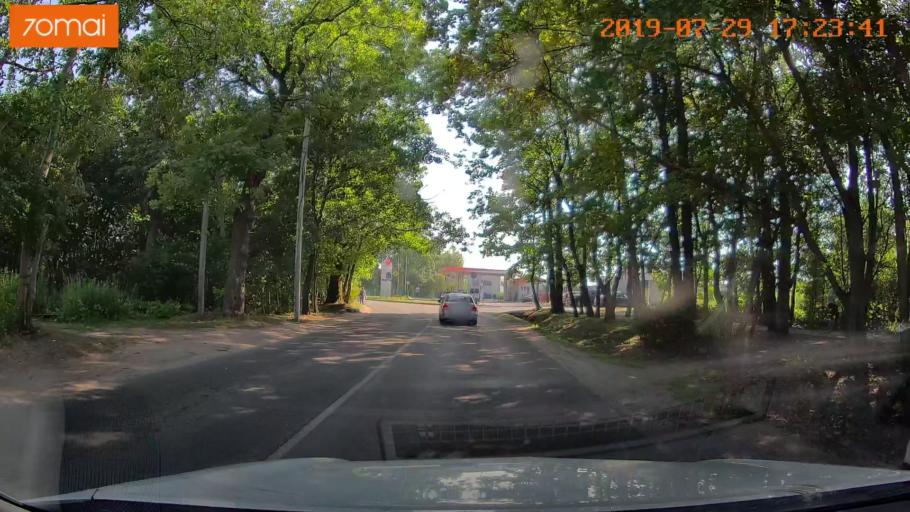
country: RU
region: Kaliningrad
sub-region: Gorod Kaliningrad
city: Kaliningrad
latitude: 54.7648
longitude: 20.4442
